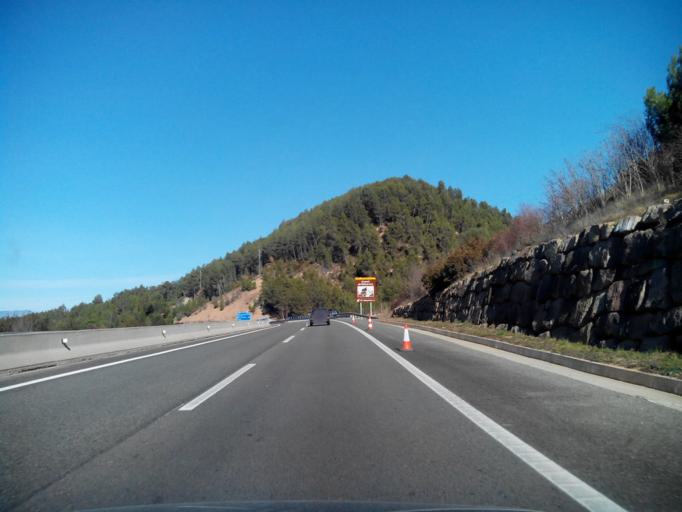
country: ES
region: Catalonia
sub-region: Provincia de Barcelona
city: Sallent
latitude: 41.8419
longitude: 1.8833
